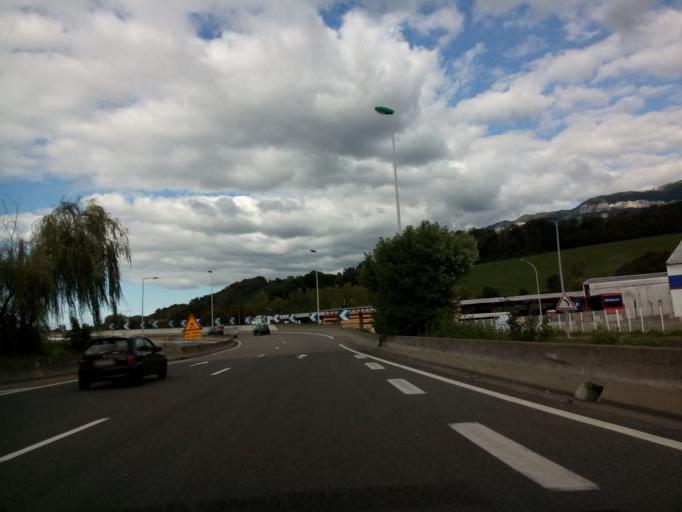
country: FR
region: Rhone-Alpes
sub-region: Departement de la Savoie
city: La Motte-Servolex
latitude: 45.6019
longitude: 5.8925
